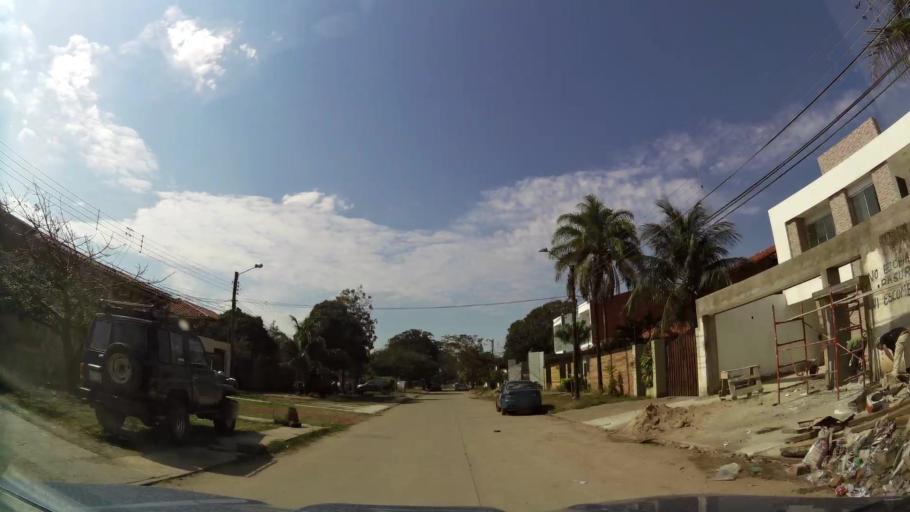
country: BO
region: Santa Cruz
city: Santa Cruz de la Sierra
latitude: -17.7513
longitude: -63.1591
